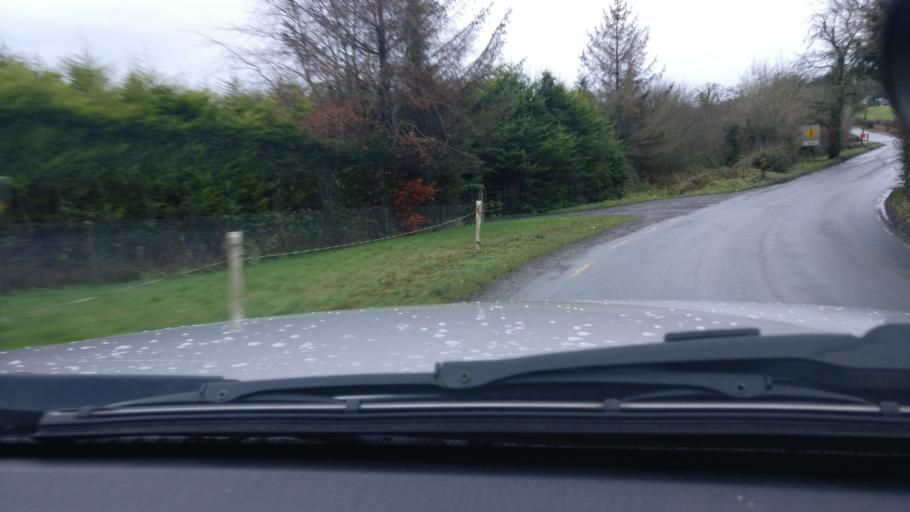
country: IE
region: Leinster
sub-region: An Longfort
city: Granard
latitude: 53.8172
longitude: -7.3582
